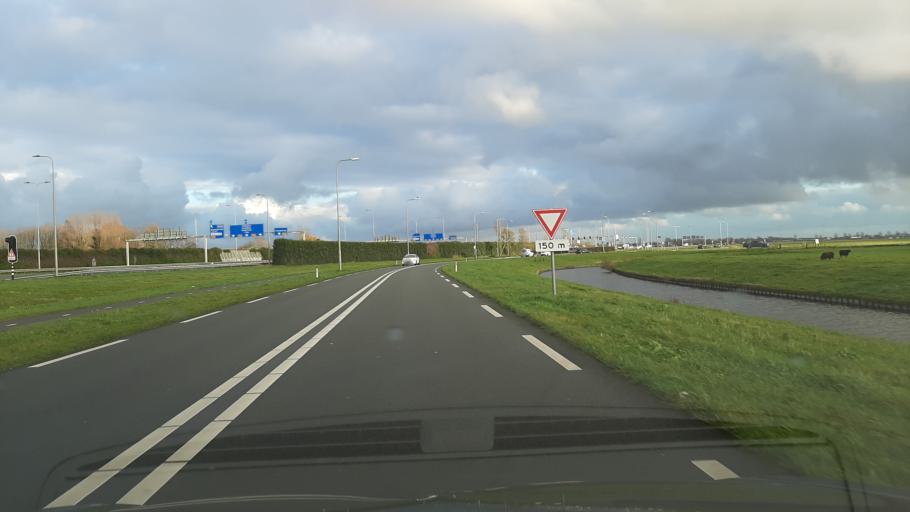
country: NL
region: North Holland
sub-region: Gemeente Haarlem
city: Haarlem
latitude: 52.3692
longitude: 4.7010
